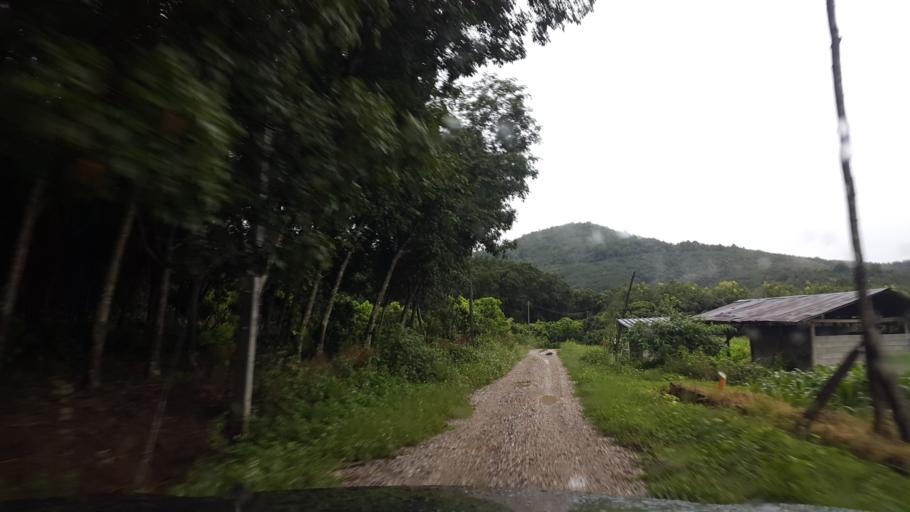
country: TH
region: Phayao
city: Phu Sang
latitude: 19.6219
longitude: 100.4086
